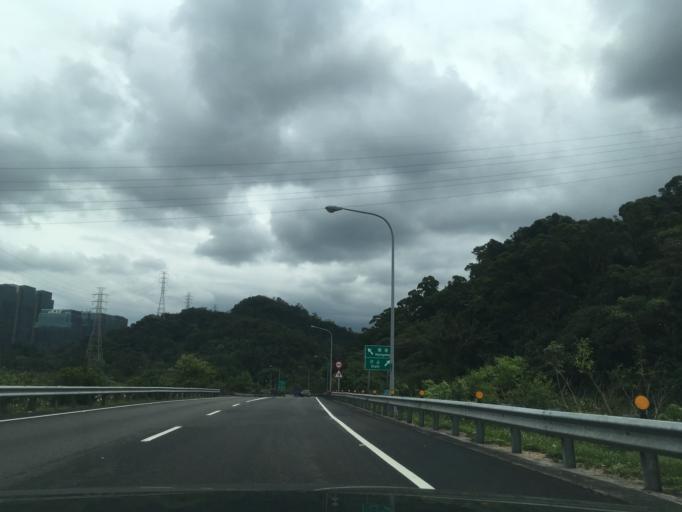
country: TW
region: Taipei
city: Taipei
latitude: 25.0551
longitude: 121.6379
